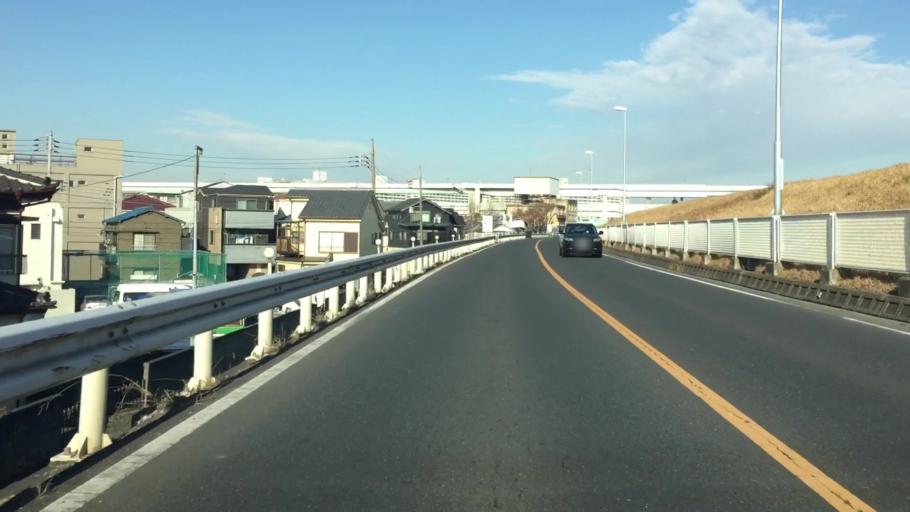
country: JP
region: Saitama
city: Kawaguchi
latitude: 35.7601
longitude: 139.7604
